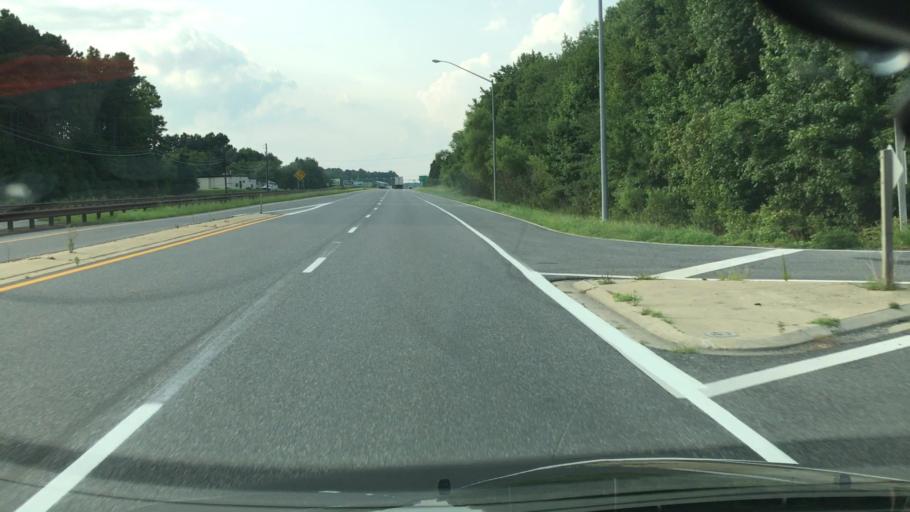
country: US
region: Delaware
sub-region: Sussex County
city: Selbyville
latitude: 38.4245
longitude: -75.2171
